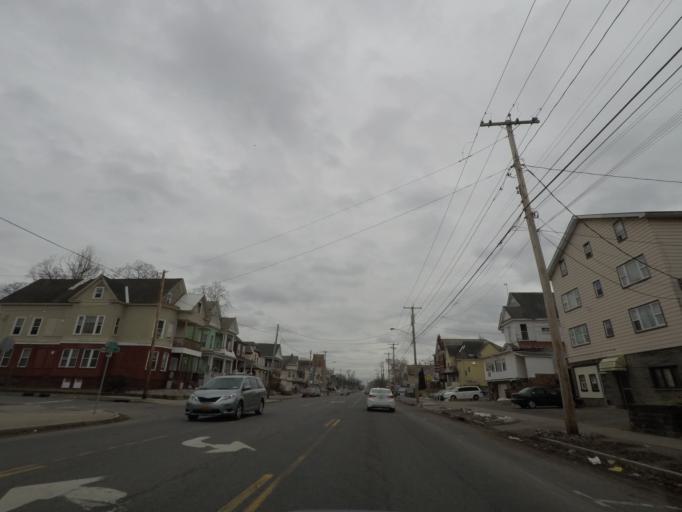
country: US
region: New York
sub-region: Schenectady County
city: Schenectady
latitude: 42.7969
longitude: -73.9226
